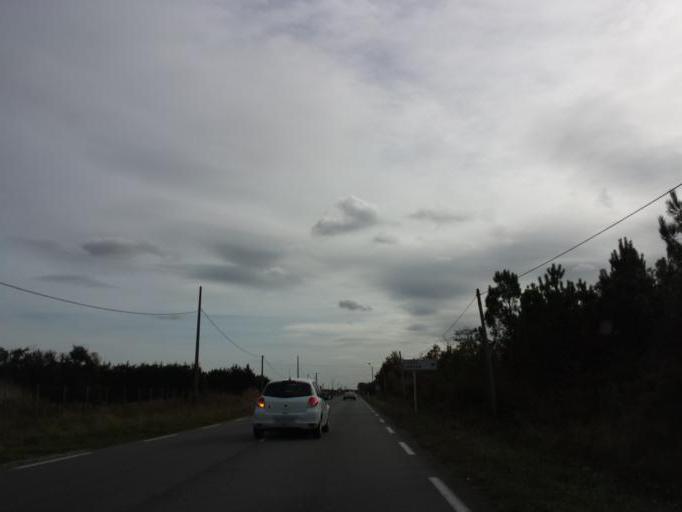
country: FR
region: Aquitaine
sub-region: Departement de la Gironde
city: Marcheprime
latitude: 44.7727
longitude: -0.9276
